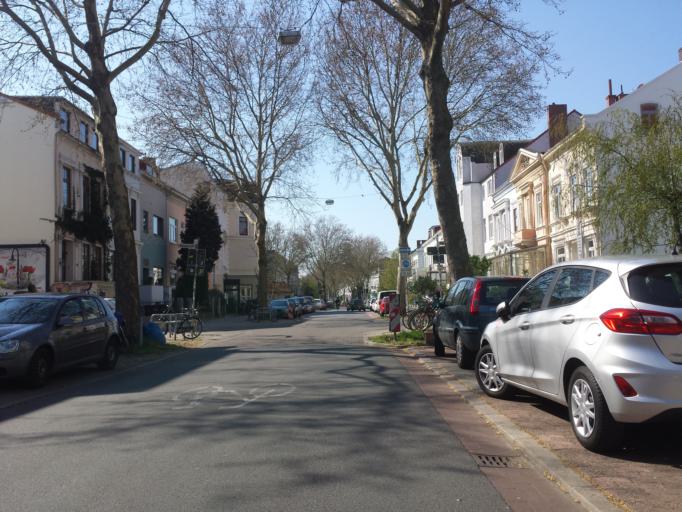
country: DE
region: Bremen
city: Bremen
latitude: 53.0748
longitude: 8.8281
